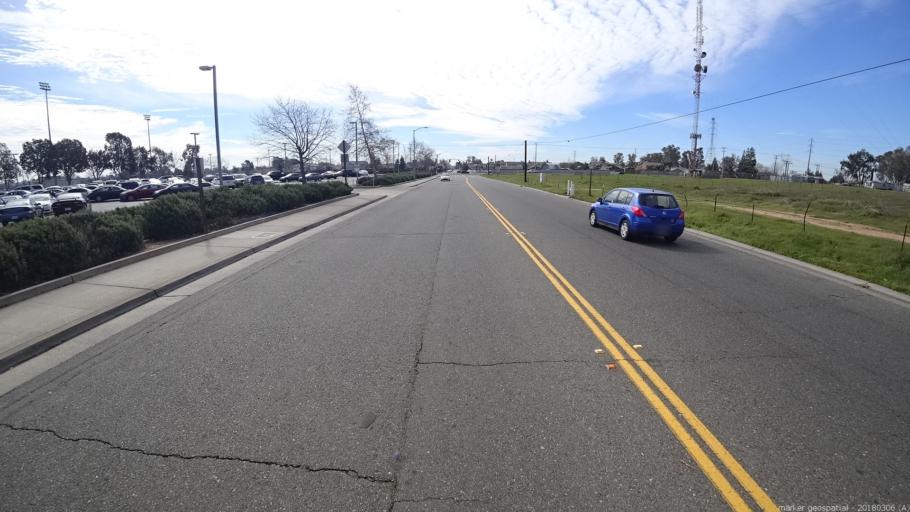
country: US
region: California
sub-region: Sacramento County
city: Vineyard
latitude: 38.4544
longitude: -121.3487
